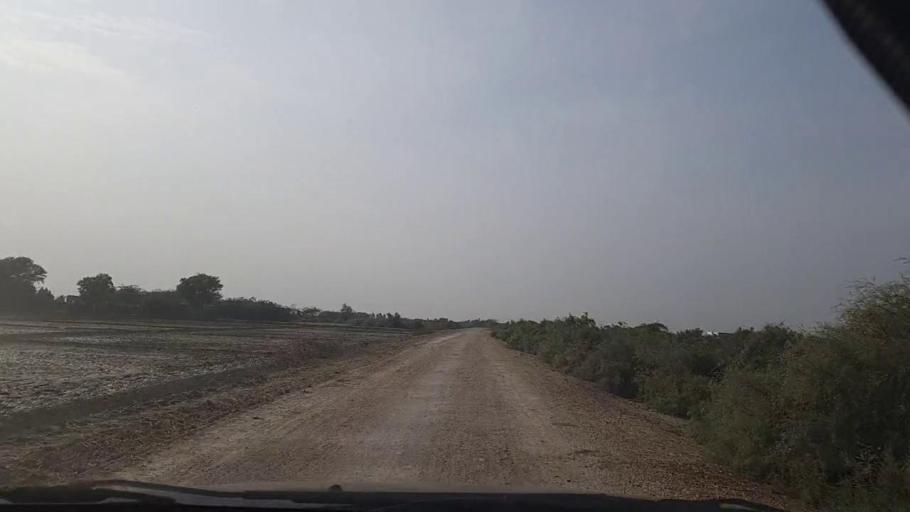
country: PK
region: Sindh
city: Thatta
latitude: 24.6135
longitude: 67.9531
